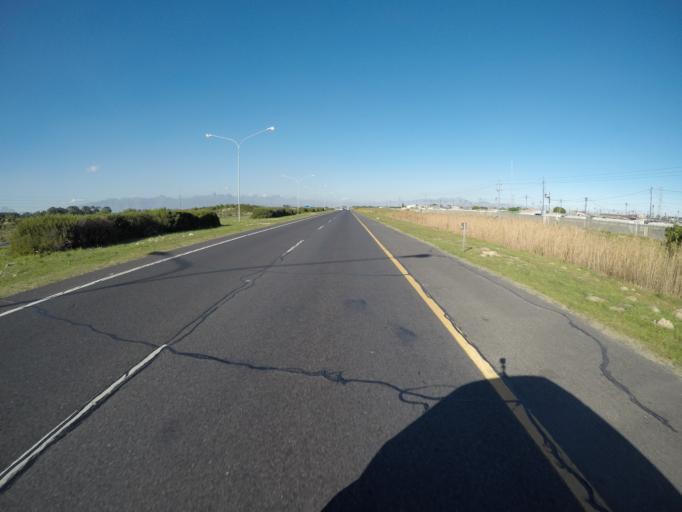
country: ZA
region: Western Cape
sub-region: City of Cape Town
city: Kraaifontein
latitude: -34.0190
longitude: 18.6728
